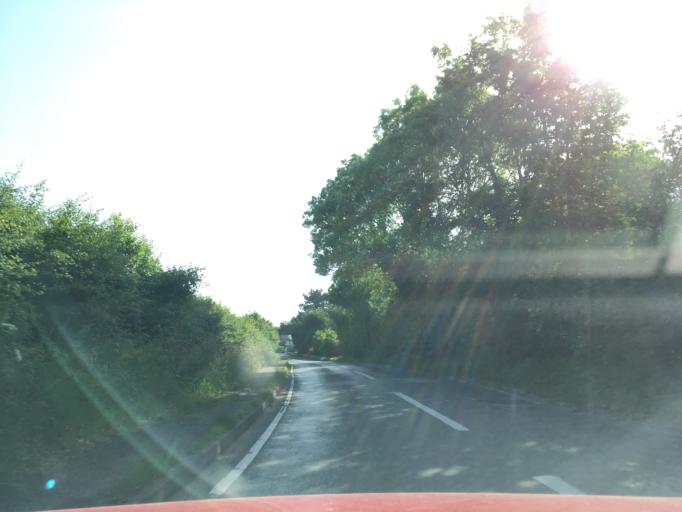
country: GB
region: England
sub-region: Oxfordshire
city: Deddington
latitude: 51.9300
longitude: -1.3584
